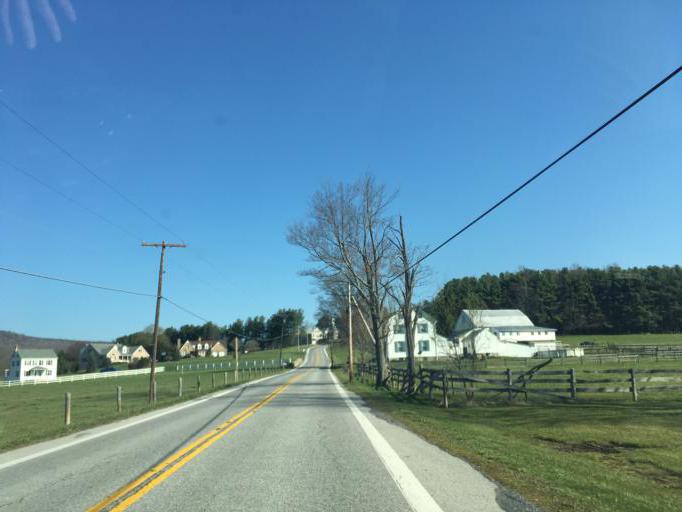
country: US
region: Maryland
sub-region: Washington County
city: Cavetown
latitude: 39.5795
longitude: -77.5564
